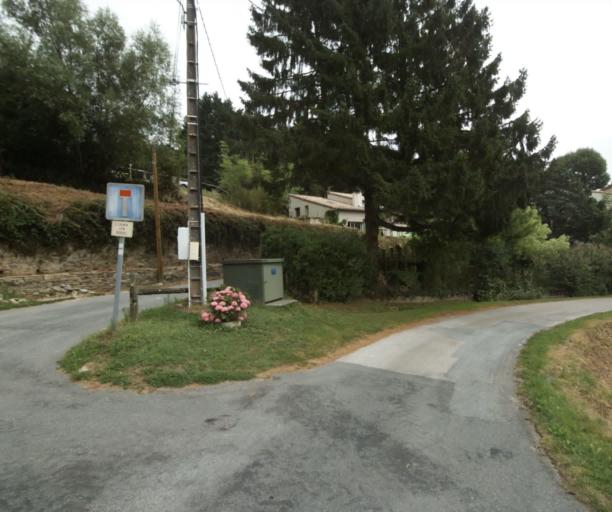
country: FR
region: Midi-Pyrenees
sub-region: Departement du Tarn
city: Soreze
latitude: 43.4137
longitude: 2.0832
